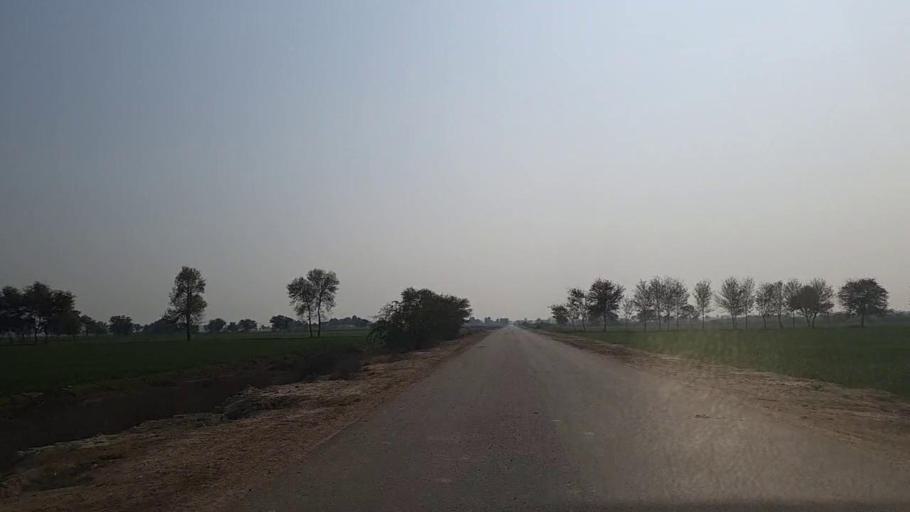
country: PK
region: Sindh
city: Jam Sahib
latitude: 26.3595
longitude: 68.5347
